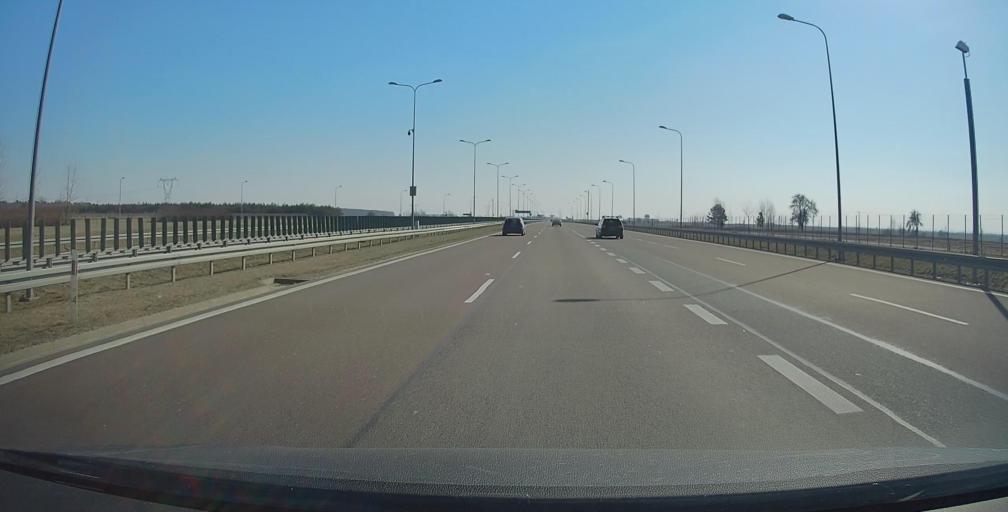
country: PL
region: Lublin Voivodeship
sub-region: Powiat pulawski
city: Kurow
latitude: 51.4340
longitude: 22.1294
